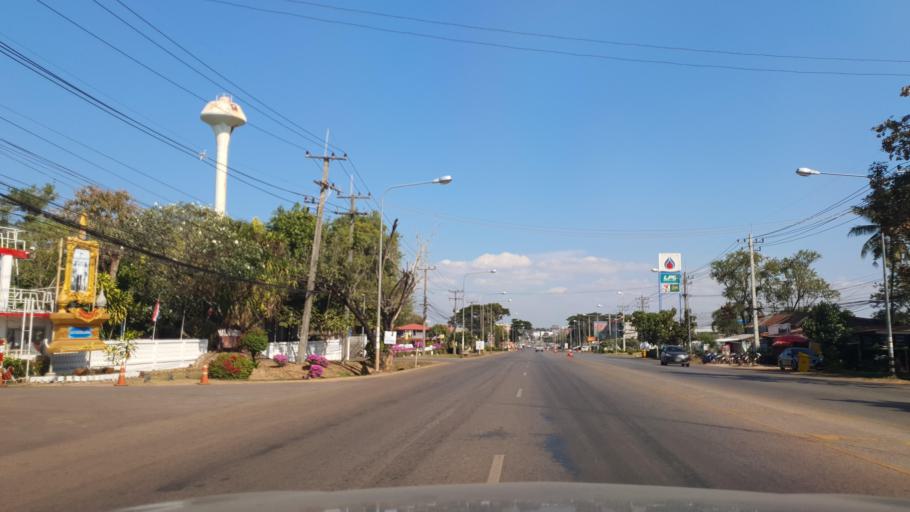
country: TH
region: Sakon Nakhon
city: Sakon Nakhon
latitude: 17.1449
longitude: 104.1207
